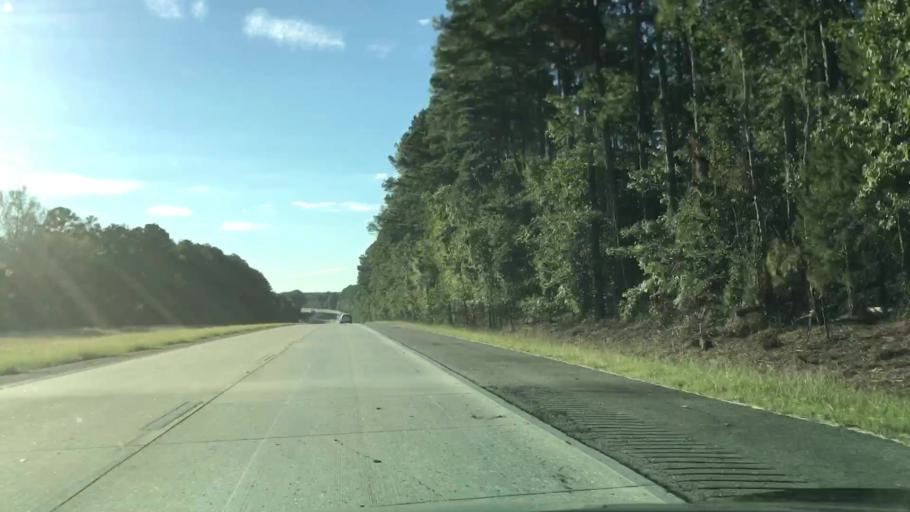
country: US
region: Georgia
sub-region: Greene County
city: Greensboro
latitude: 33.5484
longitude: -83.1201
